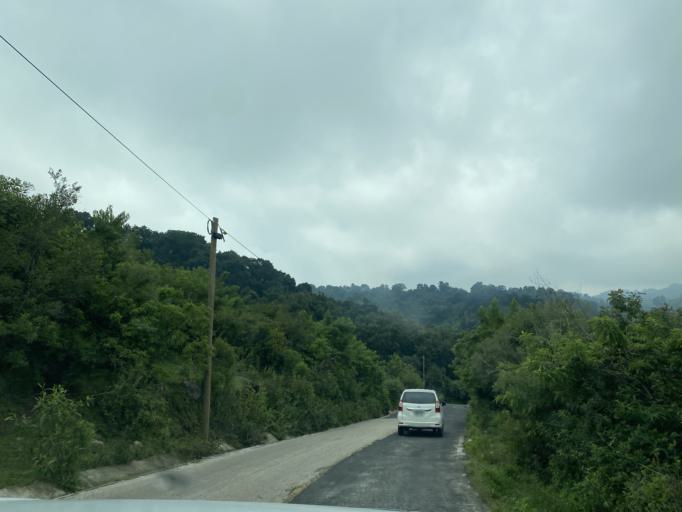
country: MX
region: Morelos
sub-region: Yecapixtla
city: Achichipico
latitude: 18.9563
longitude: -98.8272
